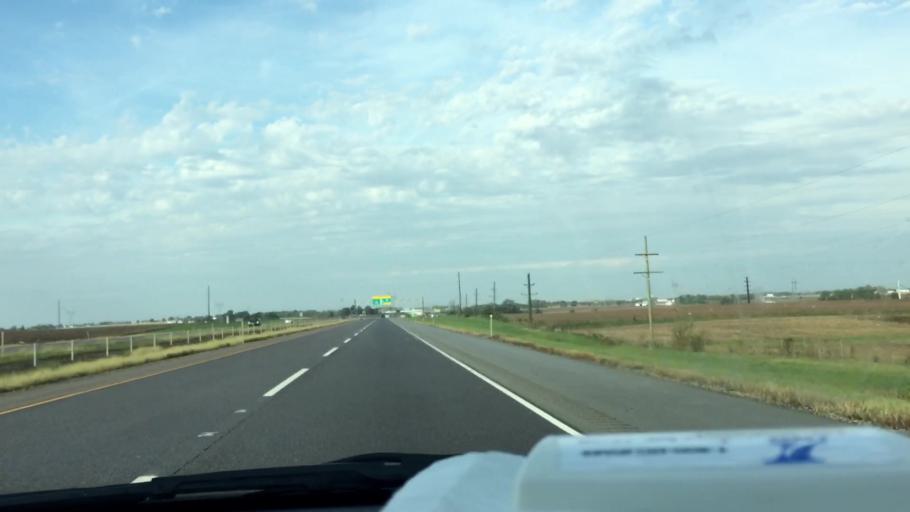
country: US
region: Illinois
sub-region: Lee County
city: Dixon
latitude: 41.8231
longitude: -89.3985
